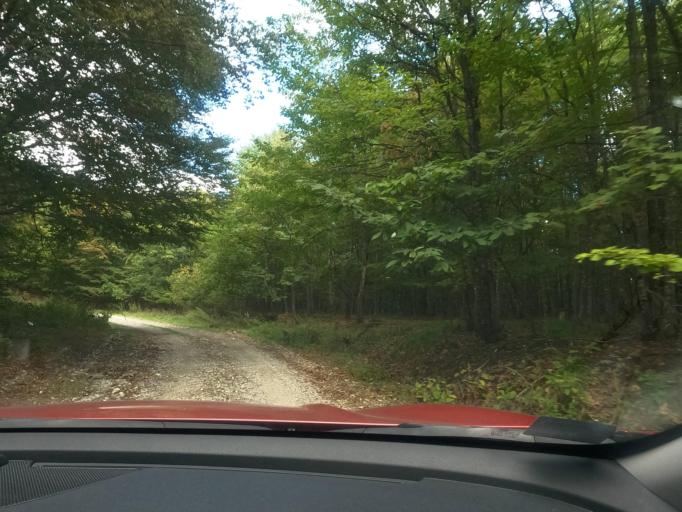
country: BA
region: Federation of Bosnia and Herzegovina
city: Velika Kladusa
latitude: 45.2591
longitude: 15.7884
